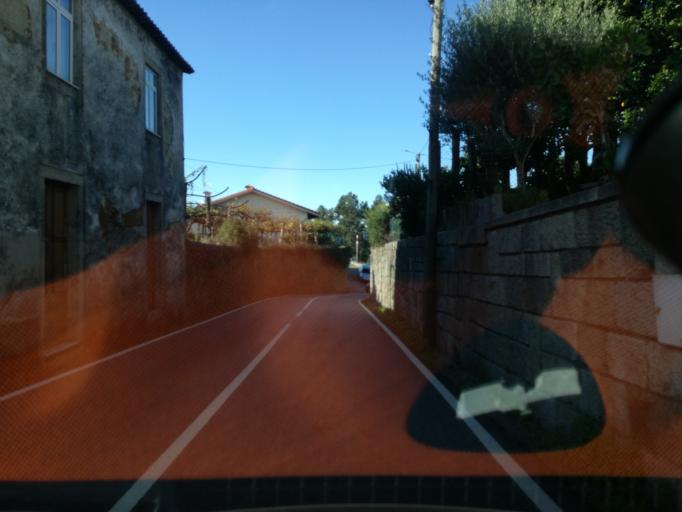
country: PT
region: Porto
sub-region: Santo Tirso
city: Sao Miguel do Couto
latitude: 41.3083
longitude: -8.4616
